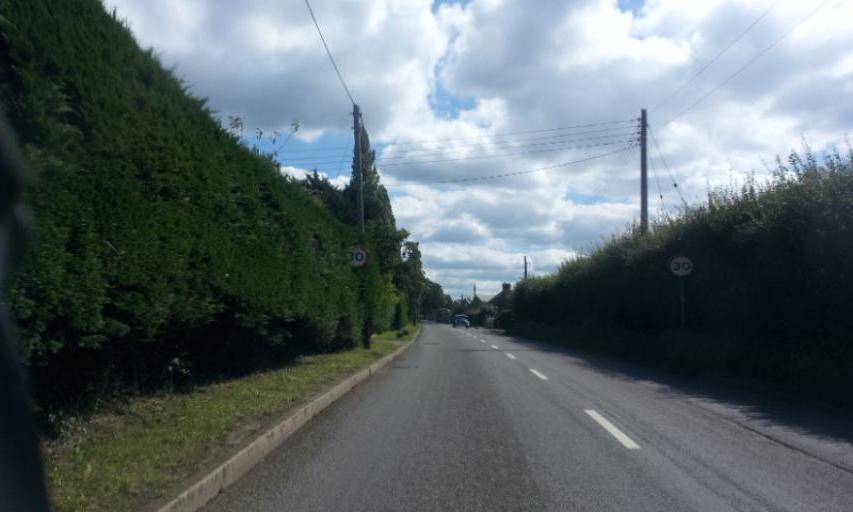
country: GB
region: England
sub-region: Kent
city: Marden
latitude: 51.1820
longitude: 0.4874
